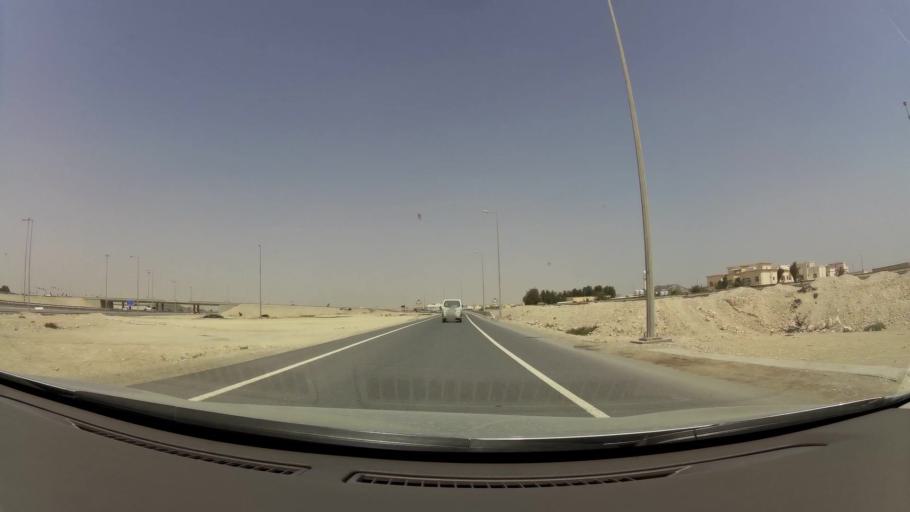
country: QA
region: Baladiyat Umm Salal
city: Umm Salal `Ali
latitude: 25.4834
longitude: 51.4080
